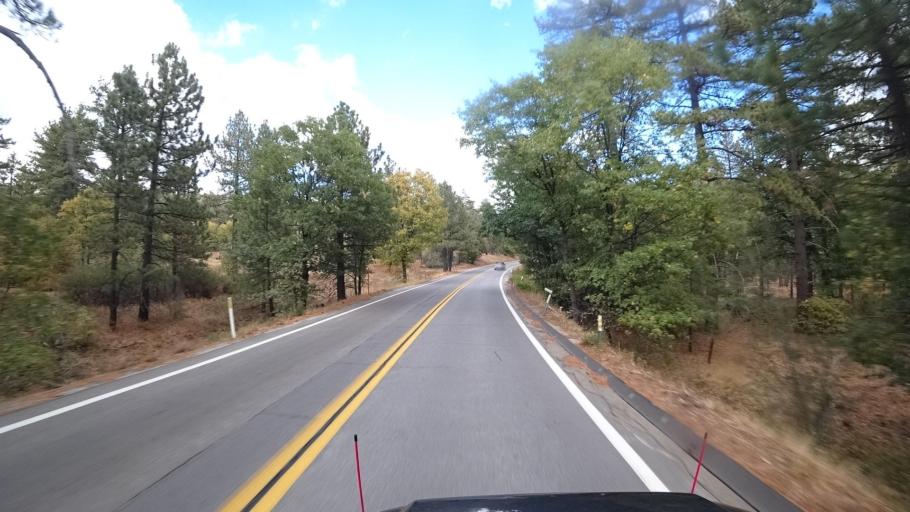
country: US
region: California
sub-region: San Diego County
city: Pine Valley
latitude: 32.8464
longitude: -116.4376
